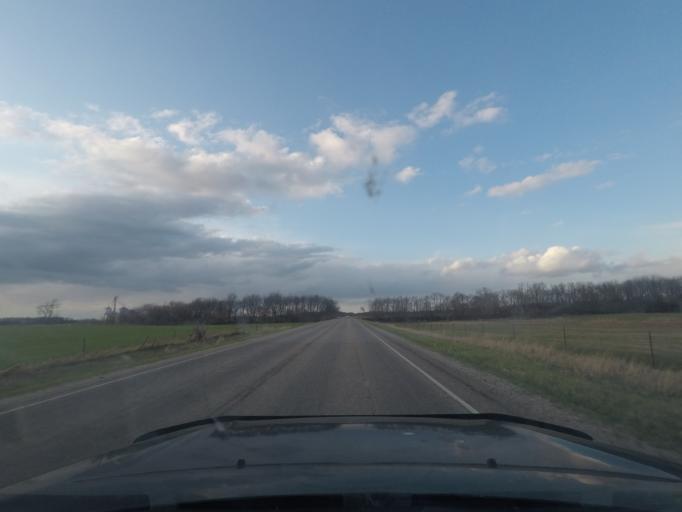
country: US
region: Indiana
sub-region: LaPorte County
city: Kingsford Heights
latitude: 41.5289
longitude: -86.7407
